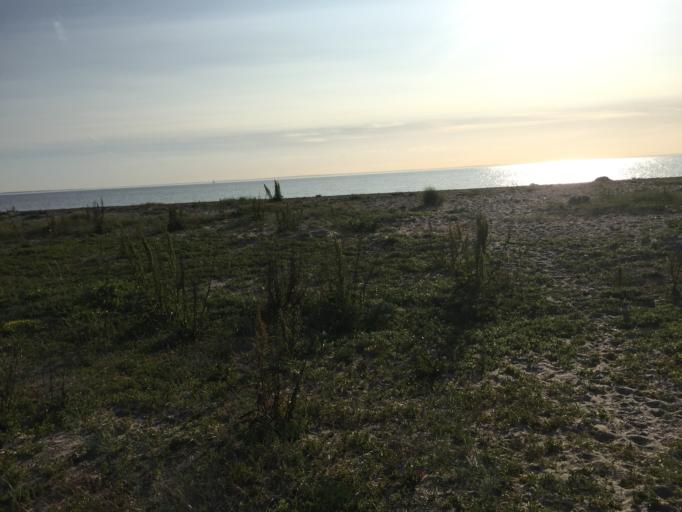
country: DK
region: Zealand
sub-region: Slagelse Kommune
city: Korsor
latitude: 55.2339
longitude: 11.1714
